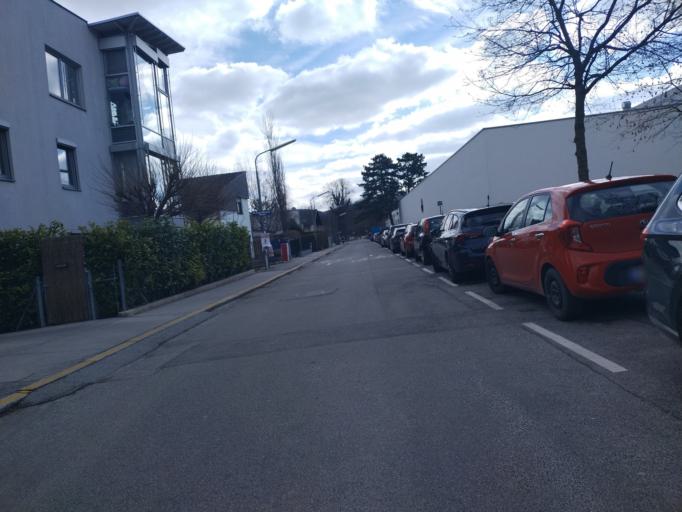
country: AT
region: Lower Austria
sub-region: Politischer Bezirk Wien-Umgebung
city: Purkersdorf
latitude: 48.2072
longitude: 16.2131
